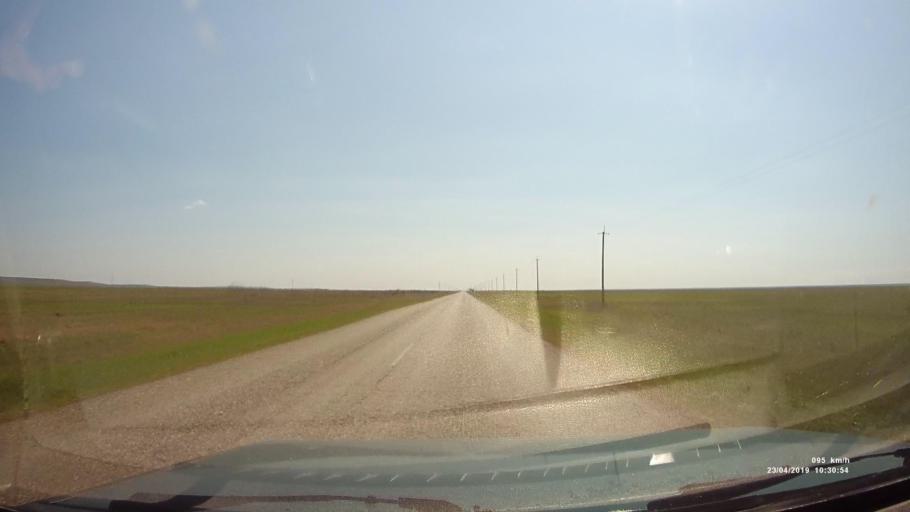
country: RU
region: Kalmykiya
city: Yashalta
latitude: 46.5891
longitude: 42.5530
